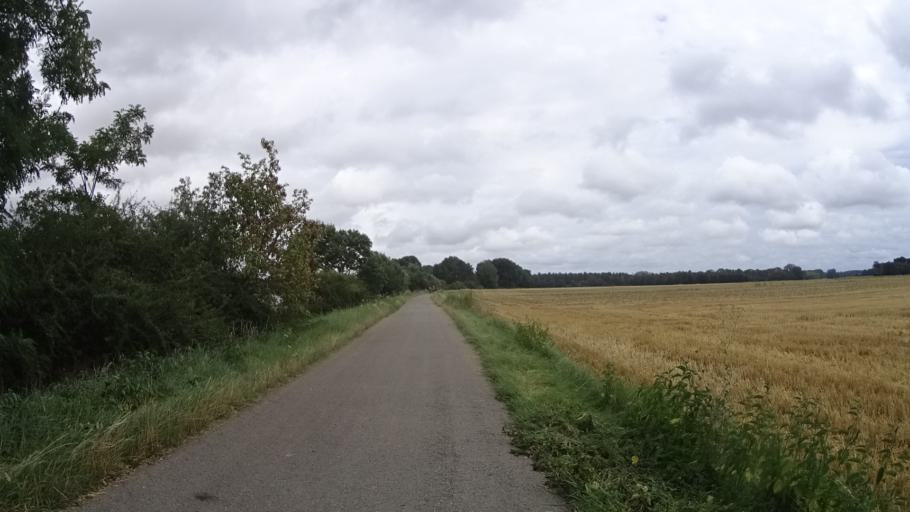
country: FR
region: Centre
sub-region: Departement du Loiret
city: Meung-sur-Loire
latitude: 47.8334
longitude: 1.7179
